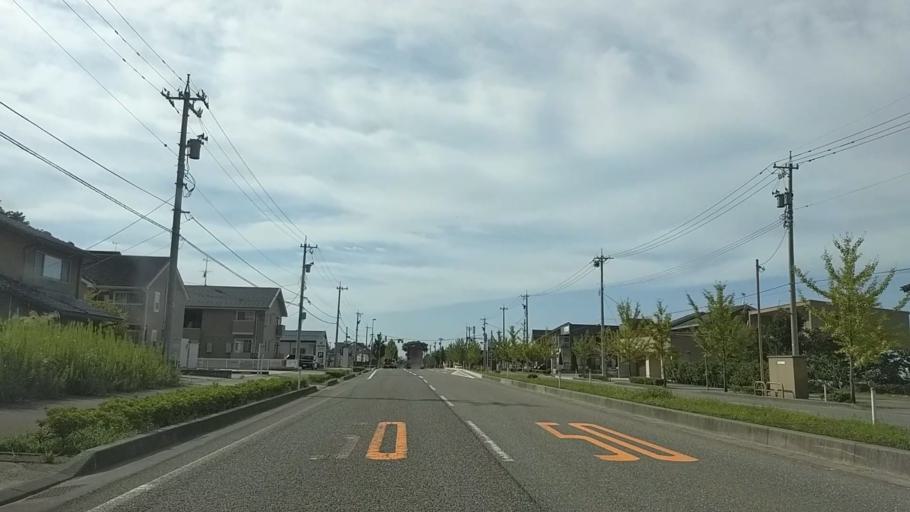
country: JP
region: Ishikawa
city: Nonoichi
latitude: 36.5344
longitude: 136.6640
